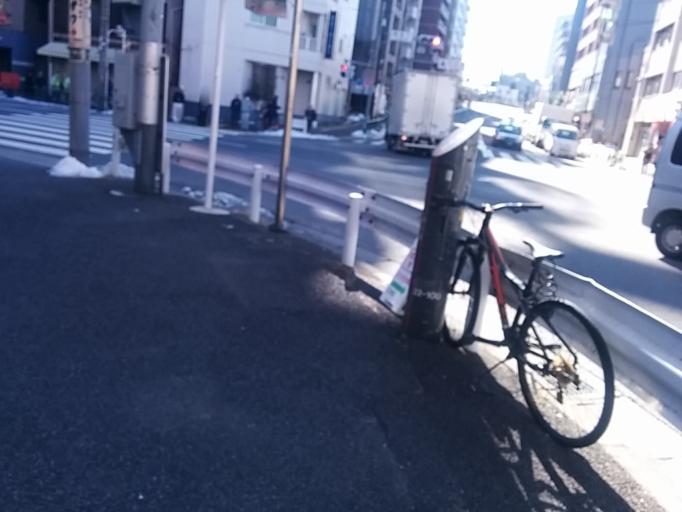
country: JP
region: Tokyo
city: Tokyo
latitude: 35.7322
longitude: 139.7585
